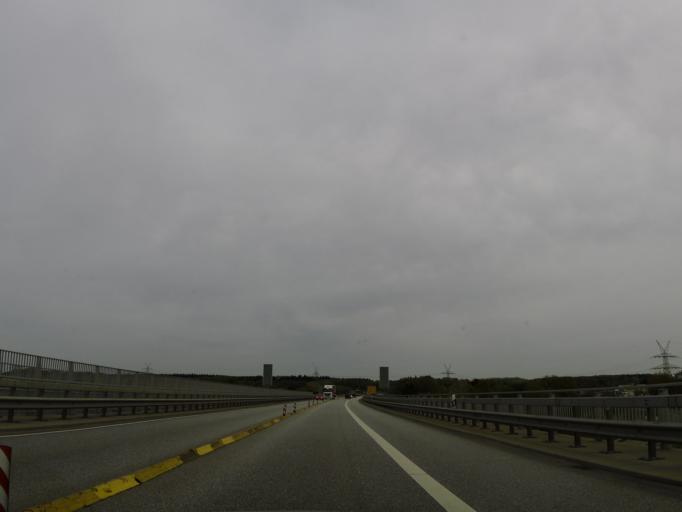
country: DE
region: Schleswig-Holstein
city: Heiligenstedten
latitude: 53.9307
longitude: 9.4808
